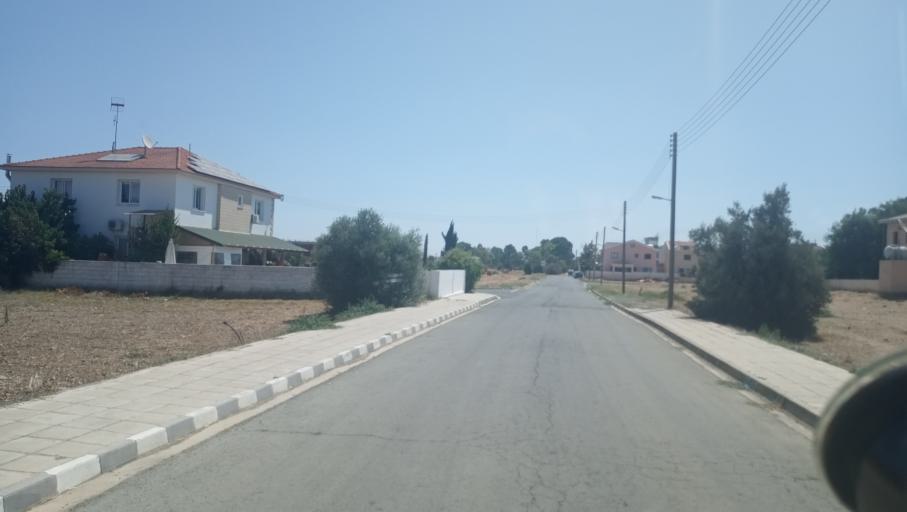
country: CY
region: Lefkosia
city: Psimolofou
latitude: 35.0640
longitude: 33.2598
